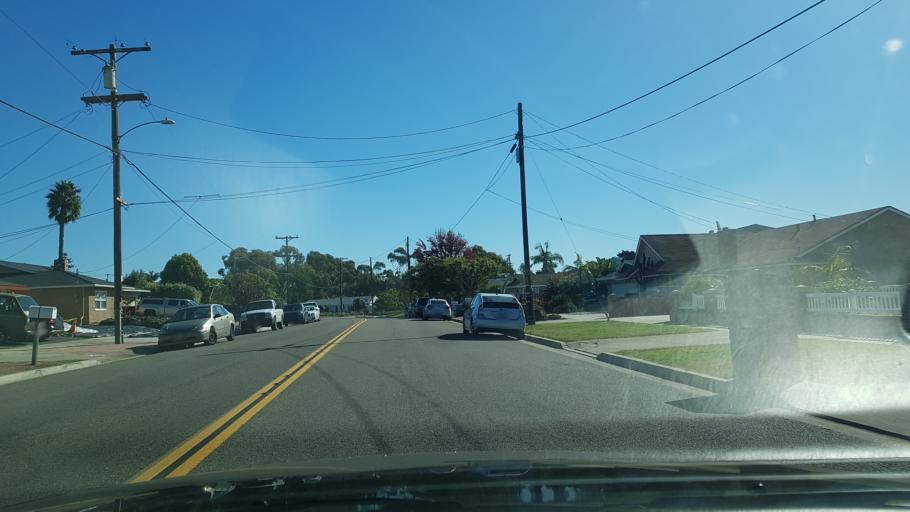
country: US
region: California
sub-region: San Diego County
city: Oceanside
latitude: 33.2048
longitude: -117.3516
